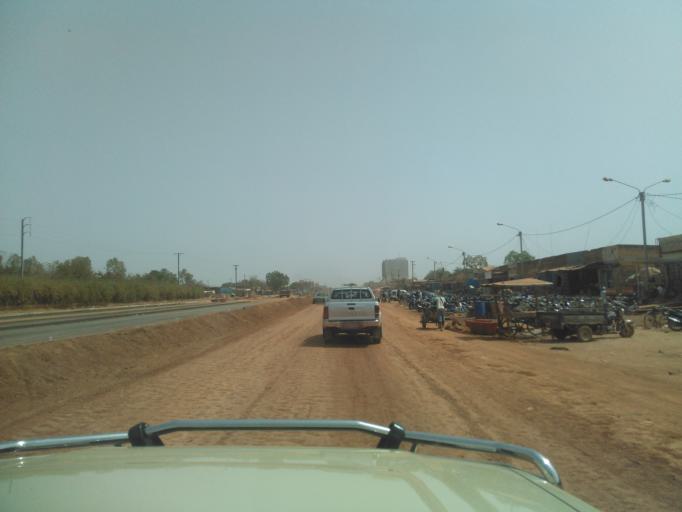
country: BF
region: Centre
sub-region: Kadiogo Province
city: Ouagadougou
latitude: 12.3905
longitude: -1.4788
